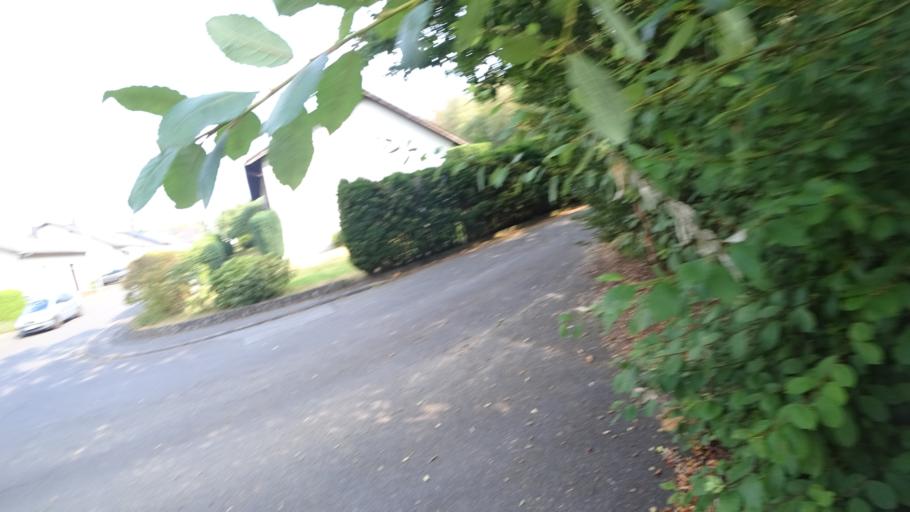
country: DE
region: Rheinland-Pfalz
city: Hilgert
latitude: 50.4533
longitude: 7.6947
